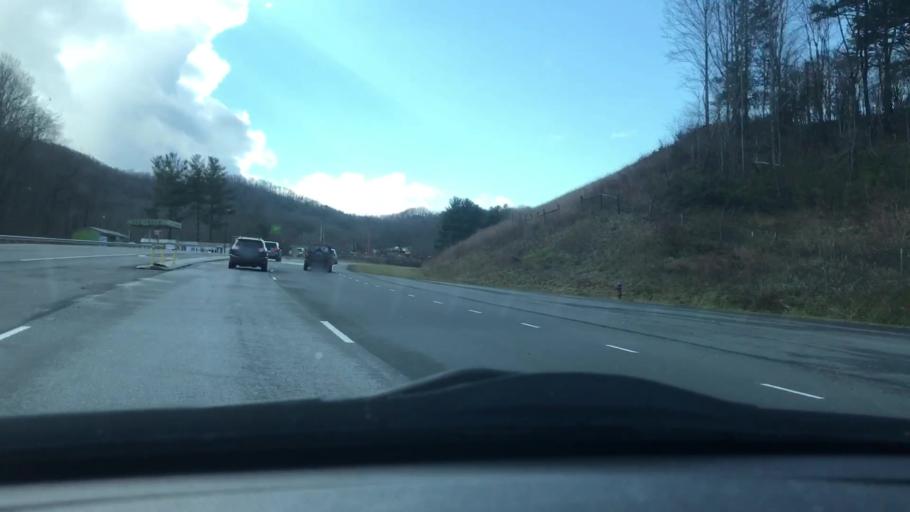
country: US
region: North Carolina
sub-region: Yancey County
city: Burnsville
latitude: 35.9137
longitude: -82.2536
